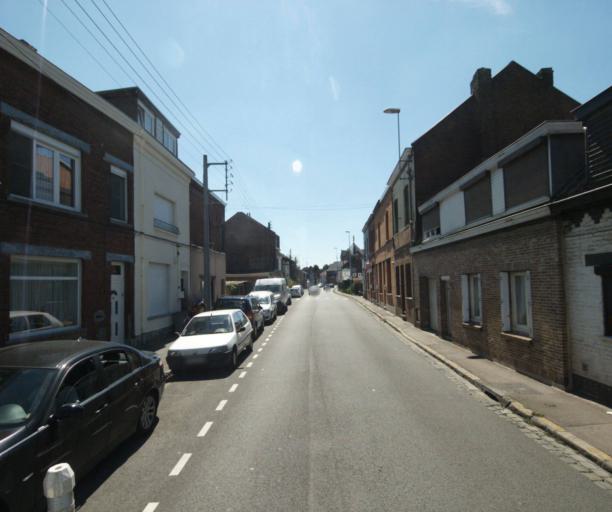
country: BE
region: Wallonia
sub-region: Province du Hainaut
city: Mouscron
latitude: 50.7367
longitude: 3.1962
